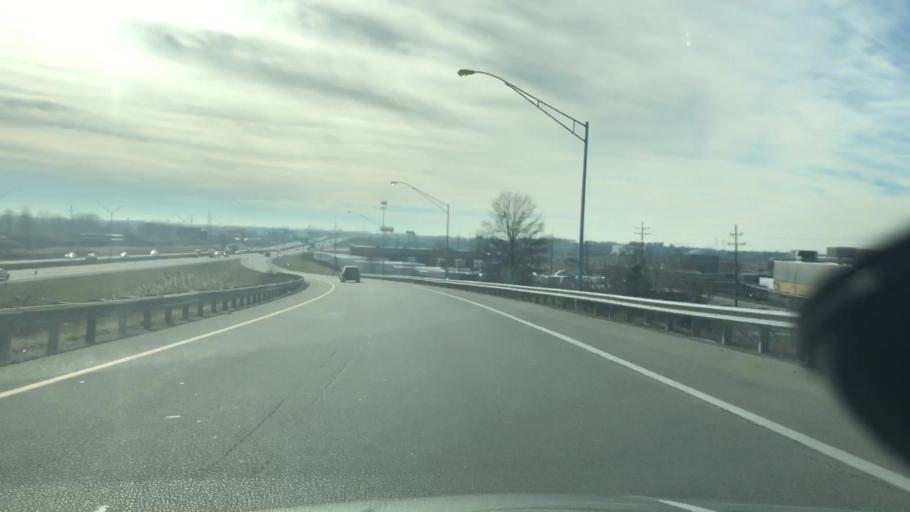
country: US
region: Ohio
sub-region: Cuyahoga County
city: Brook Park
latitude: 41.4170
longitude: -81.8185
